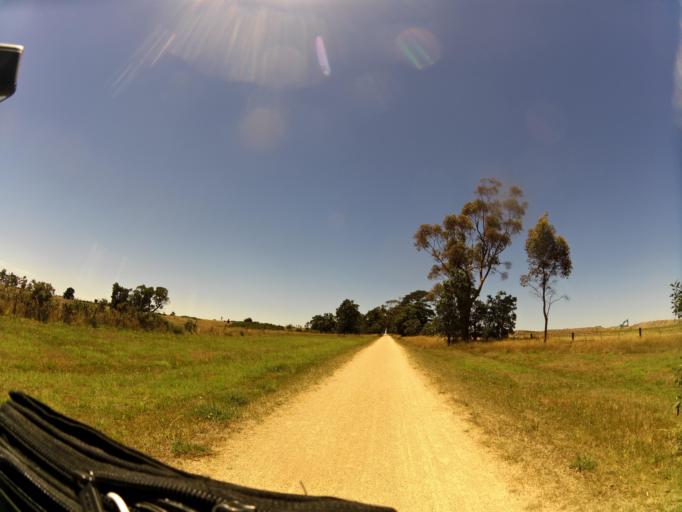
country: AU
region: Victoria
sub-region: Ballarat North
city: Newington
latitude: -37.5477
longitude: 143.7606
